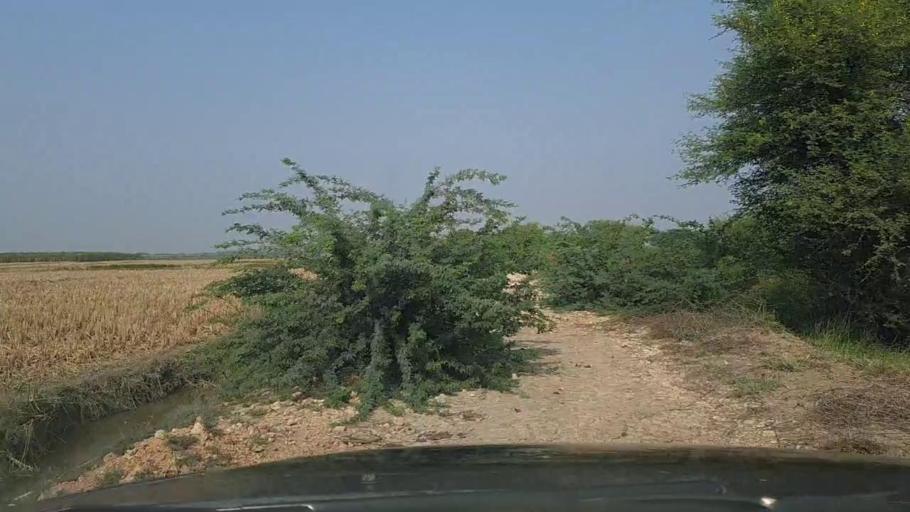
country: PK
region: Sindh
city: Mirpur Batoro
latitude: 24.6885
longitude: 68.2372
